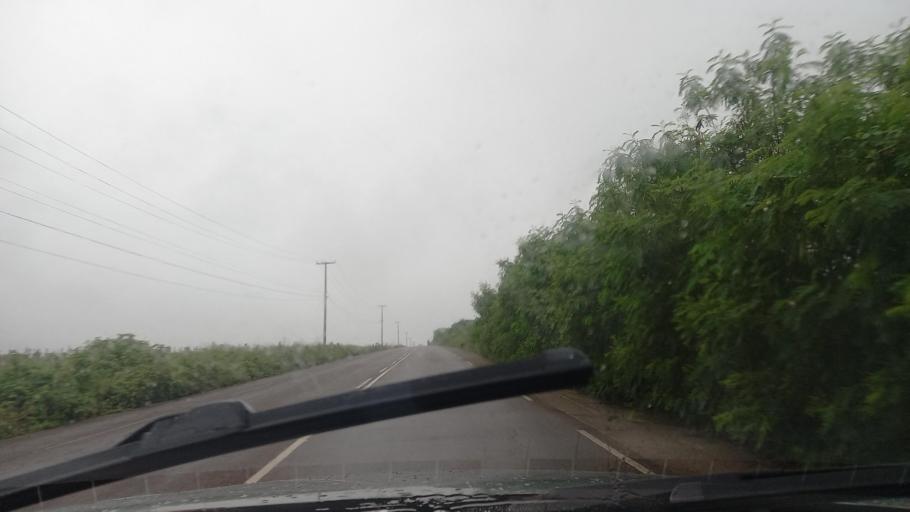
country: BR
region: Alagoas
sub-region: Lagoa Da Canoa
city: Lagoa da Canoa
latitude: -9.6980
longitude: -36.8060
